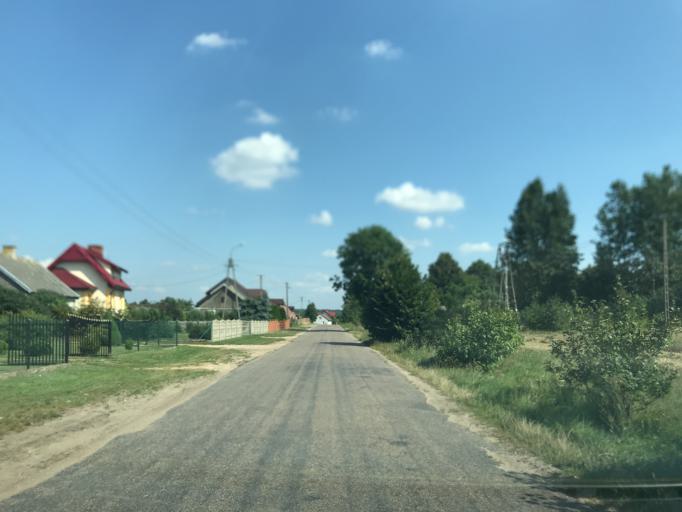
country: PL
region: Masovian Voivodeship
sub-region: Powiat zurominski
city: Lubowidz
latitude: 53.1535
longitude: 19.9275
